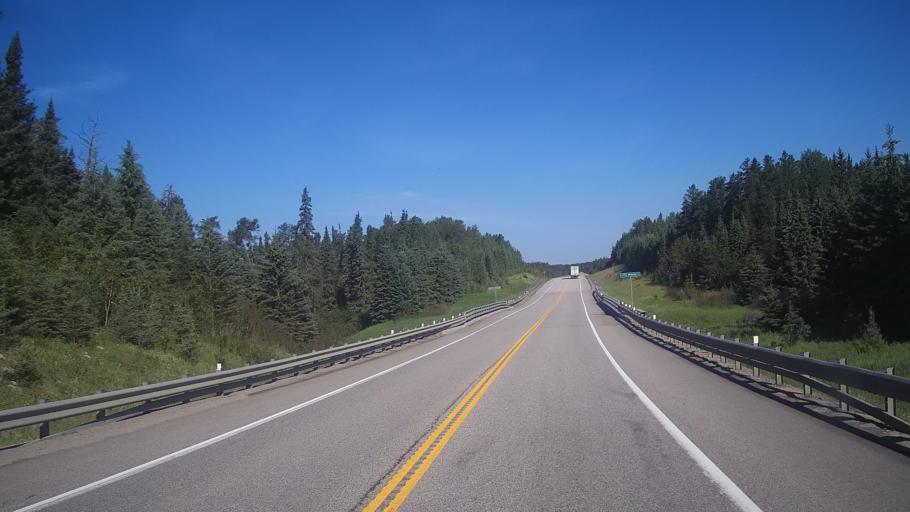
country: CA
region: Ontario
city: Dryden
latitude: 49.5674
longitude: -92.2463
